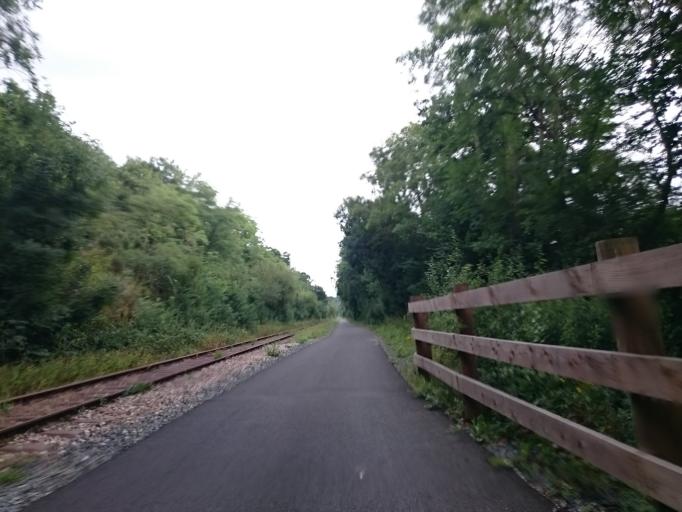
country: FR
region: Lower Normandy
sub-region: Departement du Calvados
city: Clinchamps-sur-Orne
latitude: 49.0807
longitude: -0.4260
